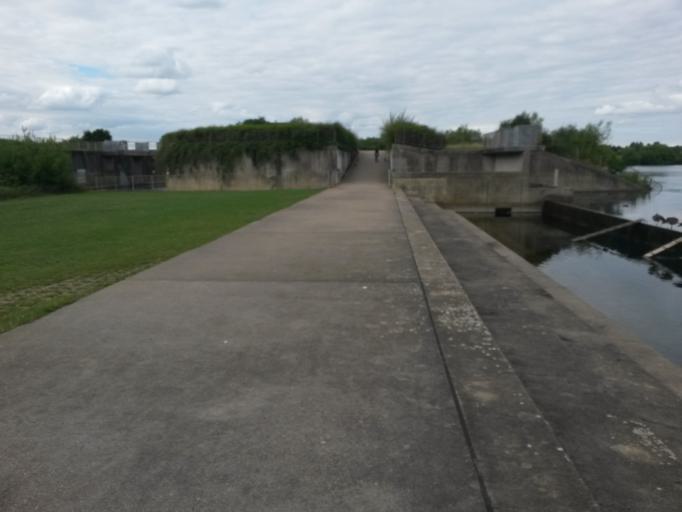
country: GB
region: England
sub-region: Milton Keynes
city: Simpson
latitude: 52.0122
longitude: -0.7104
